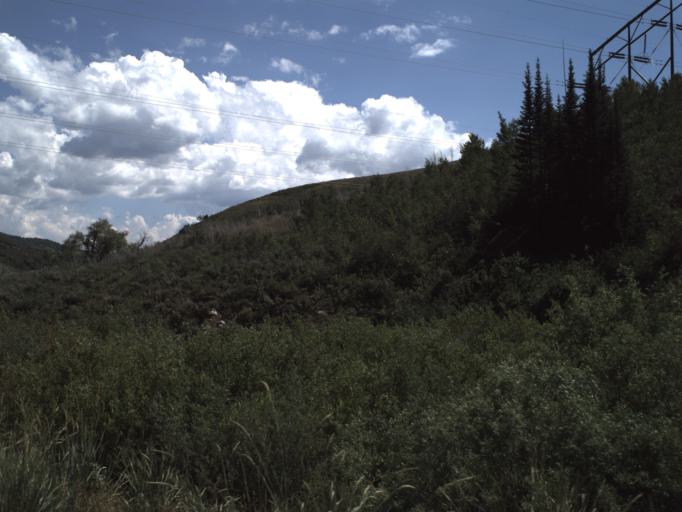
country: US
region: Utah
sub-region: Weber County
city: Wolf Creek
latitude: 41.3849
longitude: -111.5940
